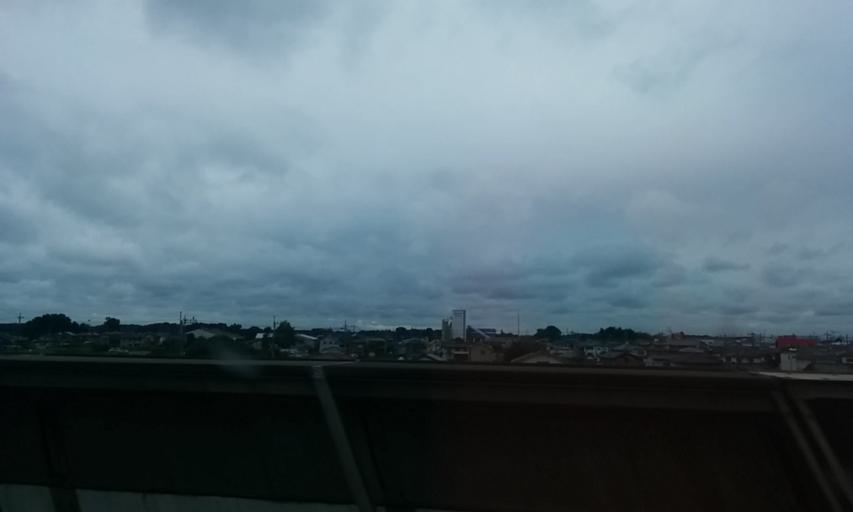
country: JP
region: Ibaraki
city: Koga
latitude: 36.2098
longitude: 139.7510
